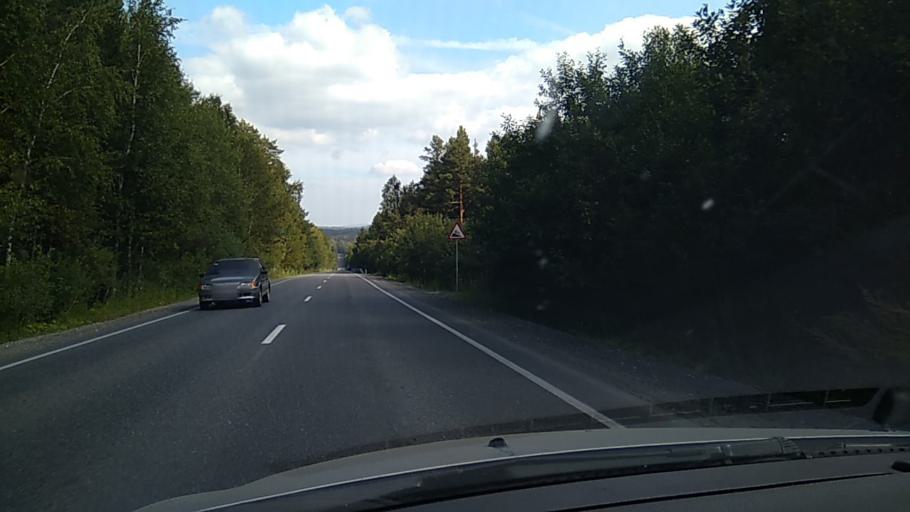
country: RU
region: Chelyabinsk
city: Syrostan
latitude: 55.1203
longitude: 59.8240
